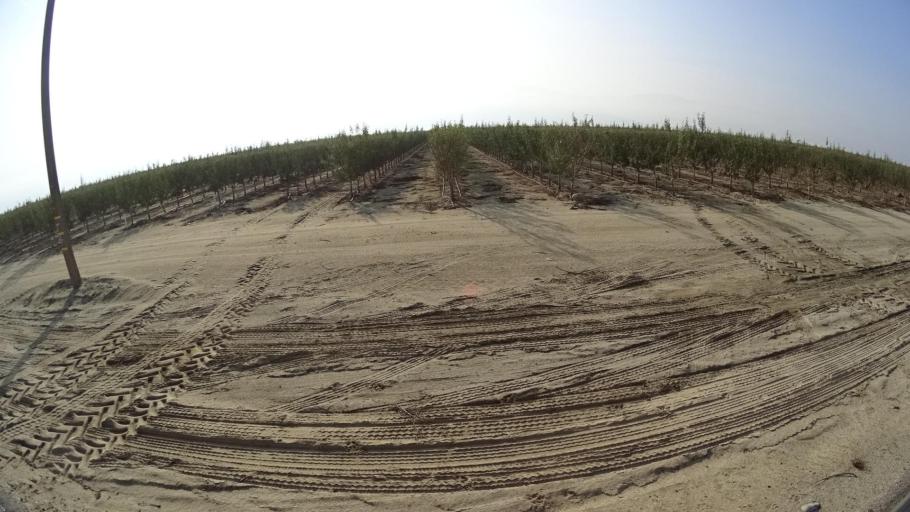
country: US
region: California
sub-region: Kern County
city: Lebec
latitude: 34.9930
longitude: -118.8843
